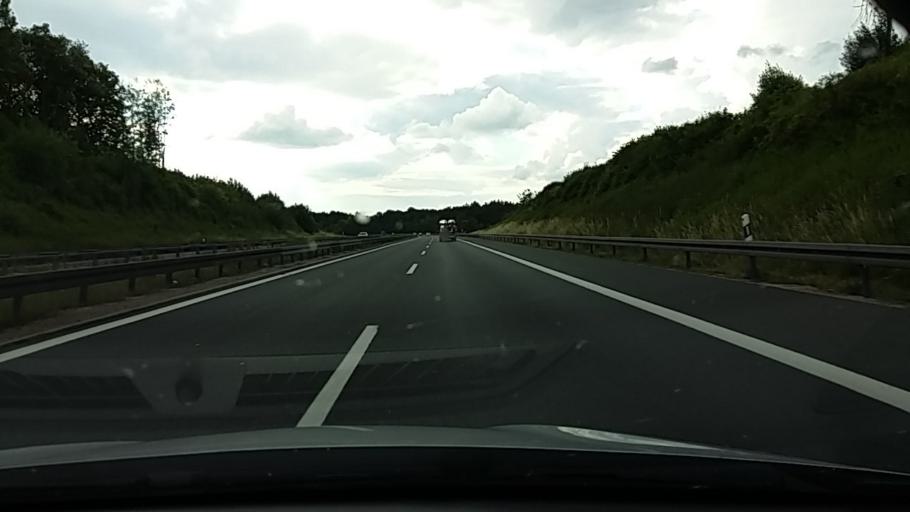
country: DE
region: Bavaria
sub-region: Upper Palatinate
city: Ursensollen
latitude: 49.4015
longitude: 11.7867
